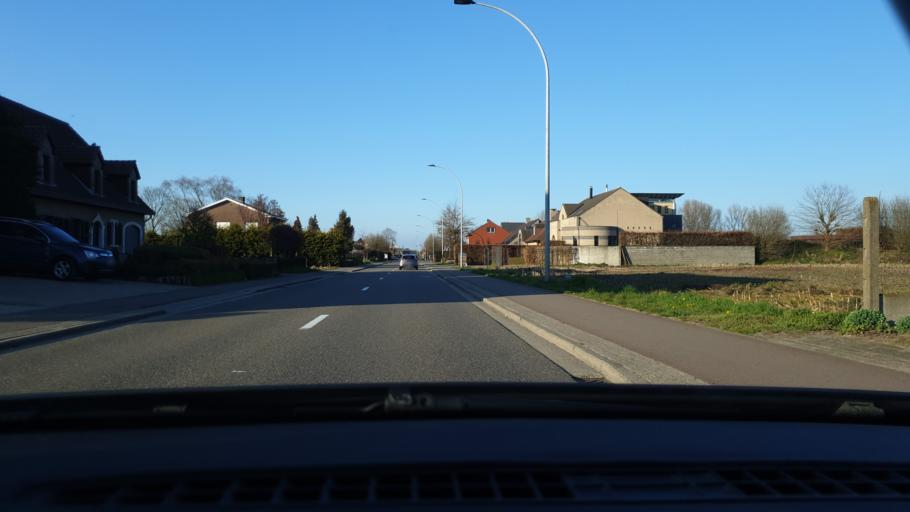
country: BE
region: Flanders
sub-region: Provincie Antwerpen
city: Geel
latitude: 51.1425
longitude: 4.9811
